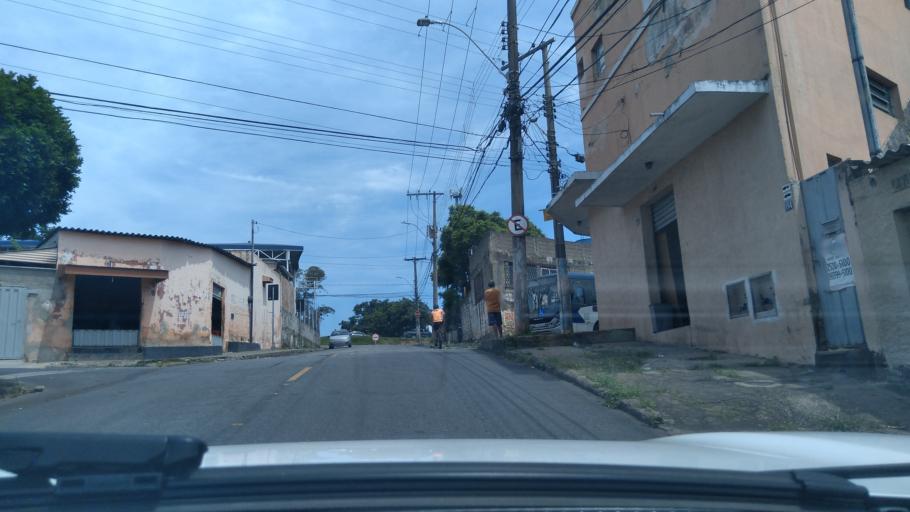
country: BR
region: Minas Gerais
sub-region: Contagem
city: Contagem
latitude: -19.9229
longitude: -44.0021
